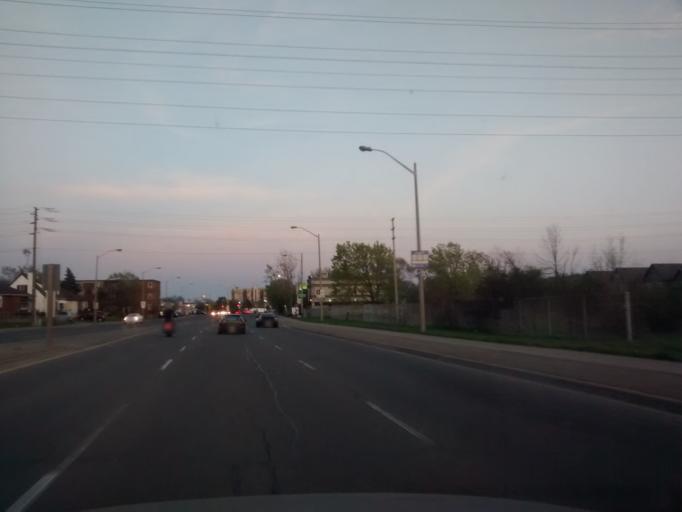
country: CA
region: Ontario
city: Burlington
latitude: 43.3406
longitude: -79.8208
